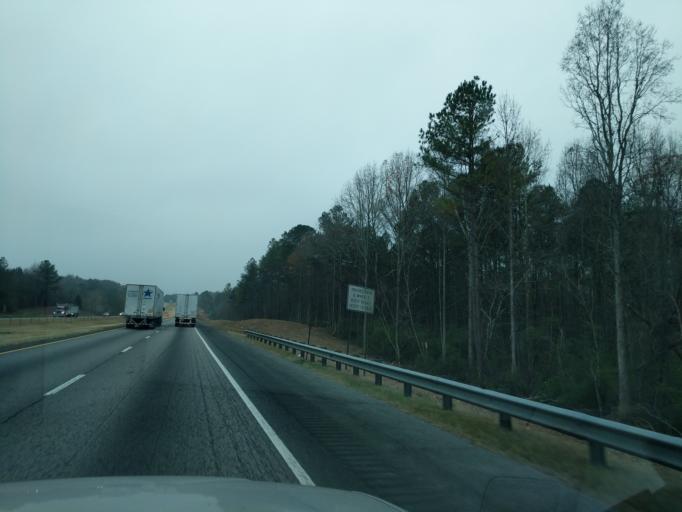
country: US
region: Georgia
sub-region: Banks County
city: Maysville
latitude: 34.2225
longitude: -83.5158
